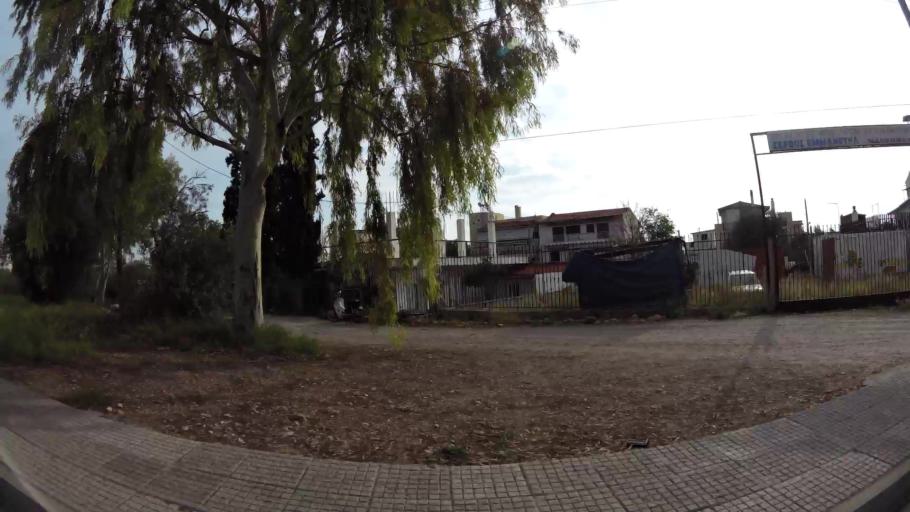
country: GR
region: Attica
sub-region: Nomarchia Athinas
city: Kamateron
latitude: 38.0558
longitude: 23.7064
